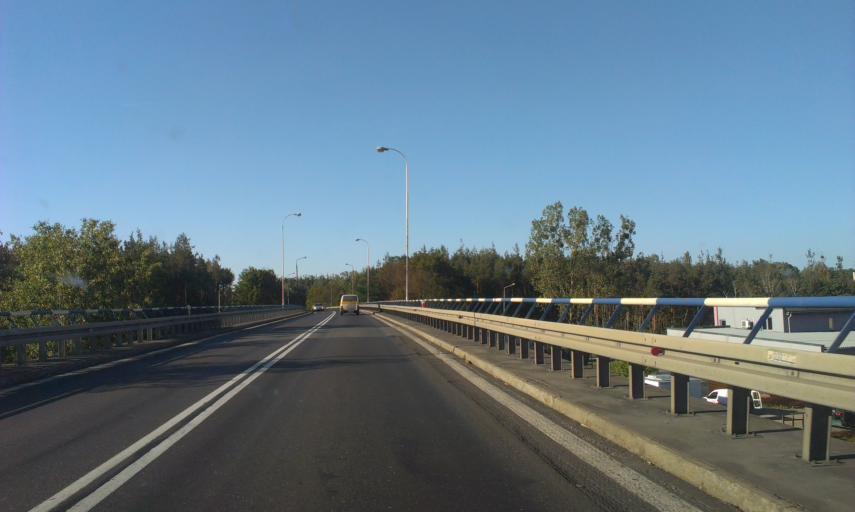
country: PL
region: Kujawsko-Pomorskie
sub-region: Powiat swiecki
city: Swiecie
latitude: 53.3990
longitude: 18.4003
